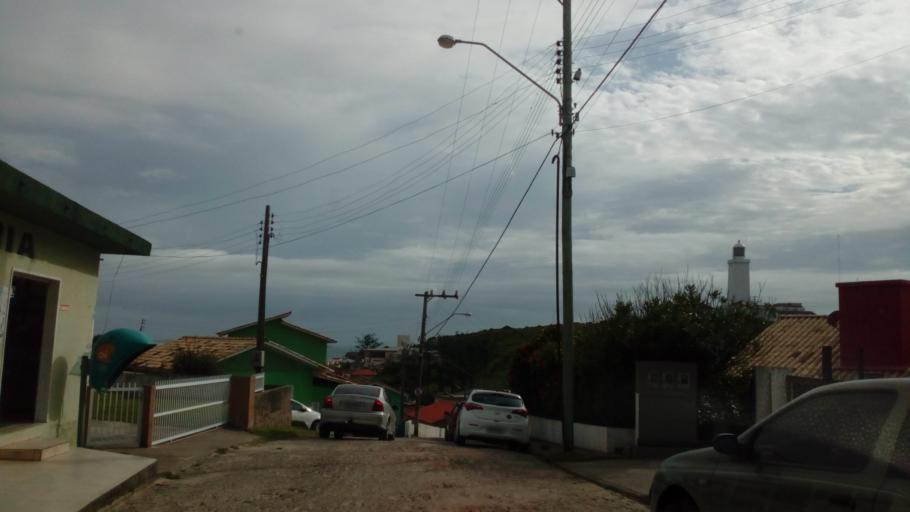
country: BR
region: Santa Catarina
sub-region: Laguna
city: Laguna
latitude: -28.6055
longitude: -48.8169
